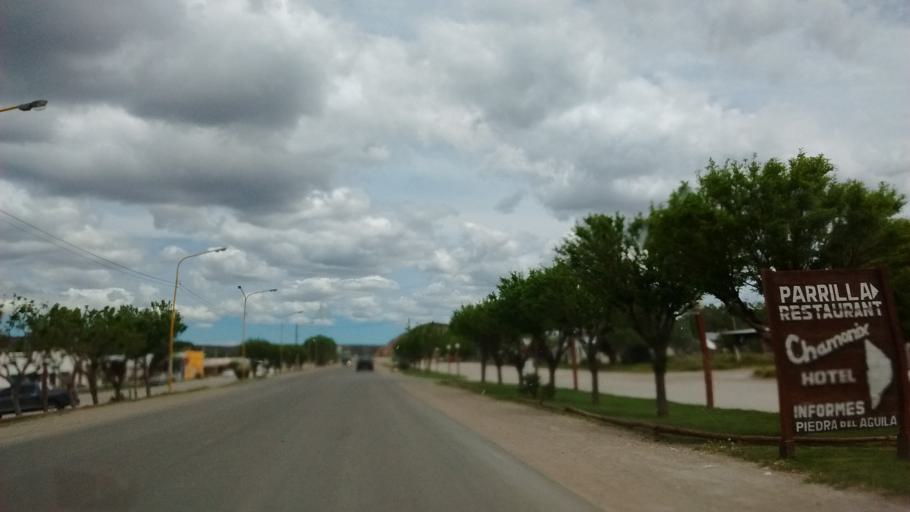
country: AR
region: Neuquen
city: Piedra del Aguila
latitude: -40.0496
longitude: -70.0778
